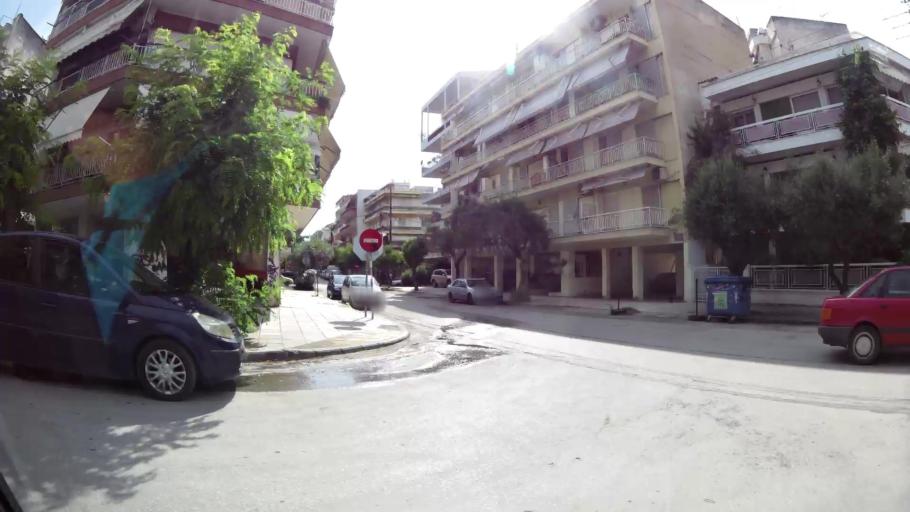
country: GR
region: Central Macedonia
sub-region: Nomos Thessalonikis
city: Kalamaria
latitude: 40.5838
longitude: 22.9662
